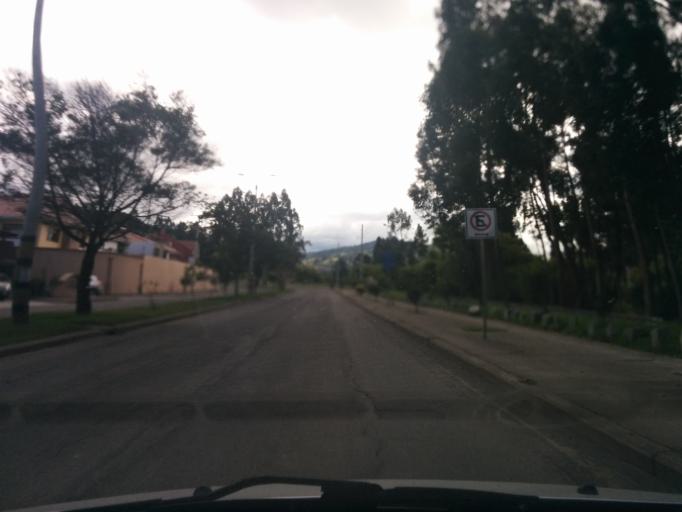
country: EC
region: Azuay
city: Cuenca
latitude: -2.9198
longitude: -79.0266
